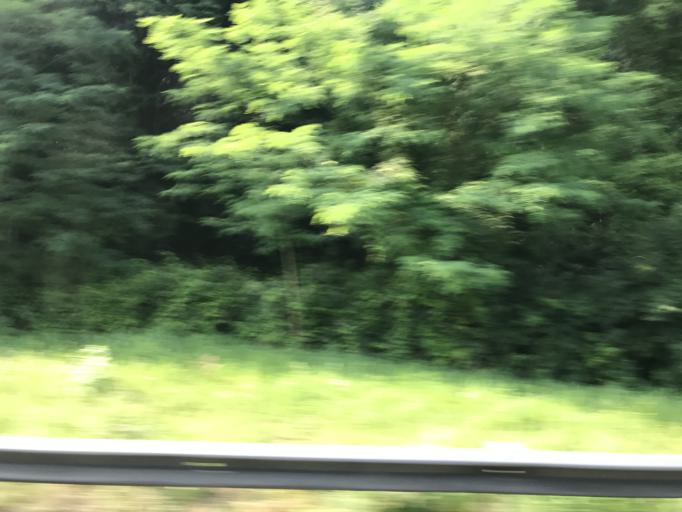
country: ES
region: Basque Country
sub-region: Provincia de Guipuzcoa
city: Legorreta
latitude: 43.0785
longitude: -2.1564
